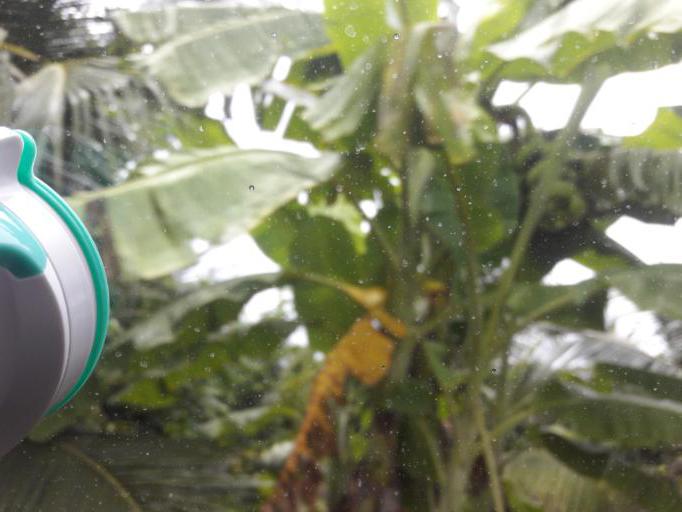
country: TH
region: Ratchaburi
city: Damnoen Saduak
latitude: 13.5286
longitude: 100.0160
